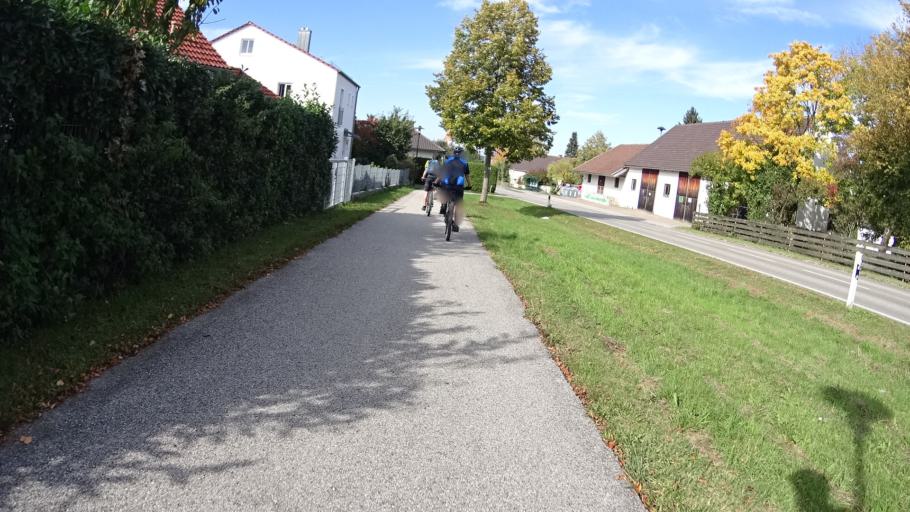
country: DE
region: Bavaria
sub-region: Upper Bavaria
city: Bohmfeld
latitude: 48.8577
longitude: 11.3693
